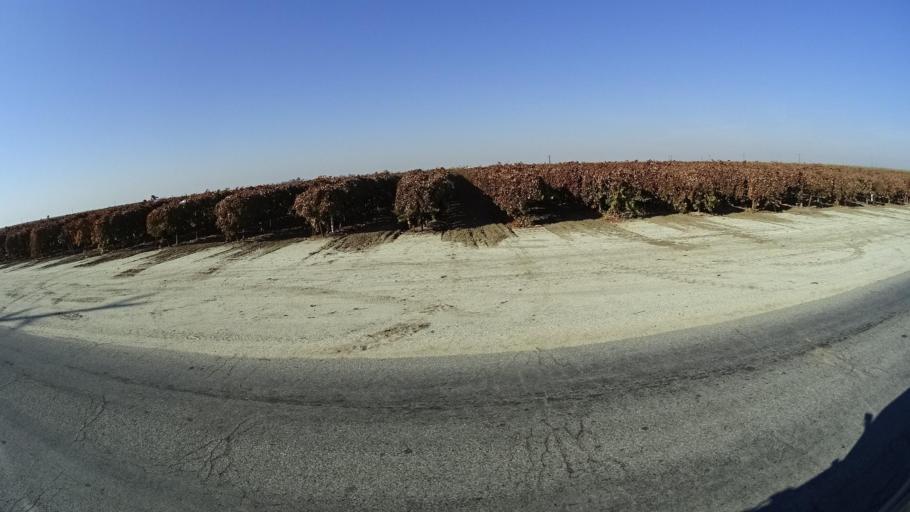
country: US
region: California
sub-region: Kern County
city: Delano
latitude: 35.7660
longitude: -119.2052
